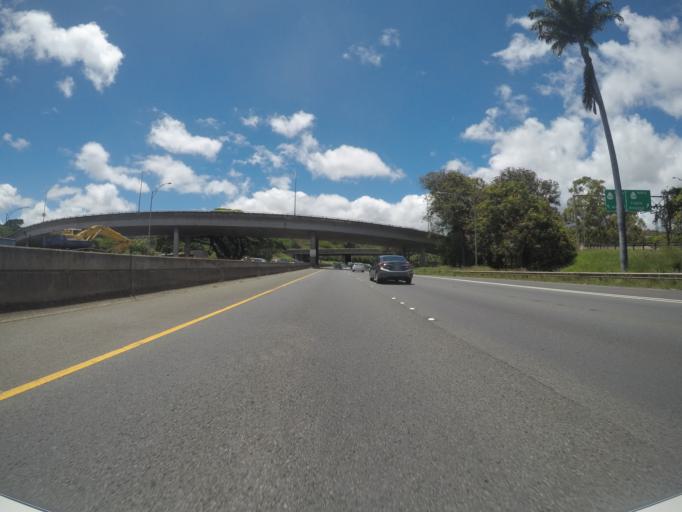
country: US
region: Hawaii
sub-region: Honolulu County
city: Halawa Heights
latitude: 21.3479
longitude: -157.8951
